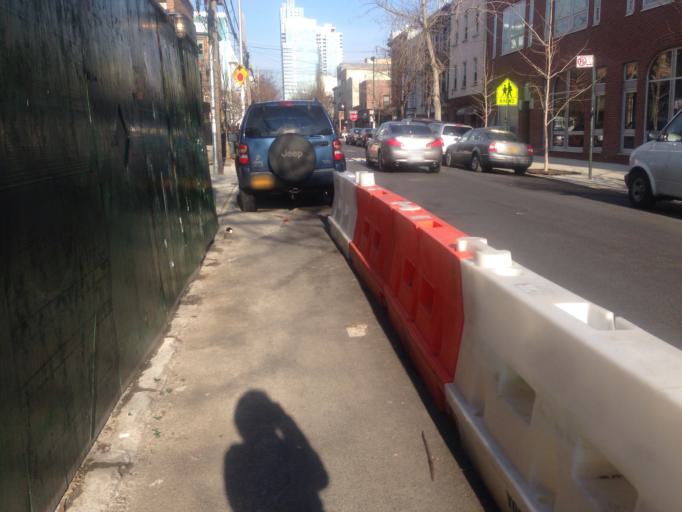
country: US
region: New York
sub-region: Queens County
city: Long Island City
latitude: 40.7157
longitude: -73.9588
